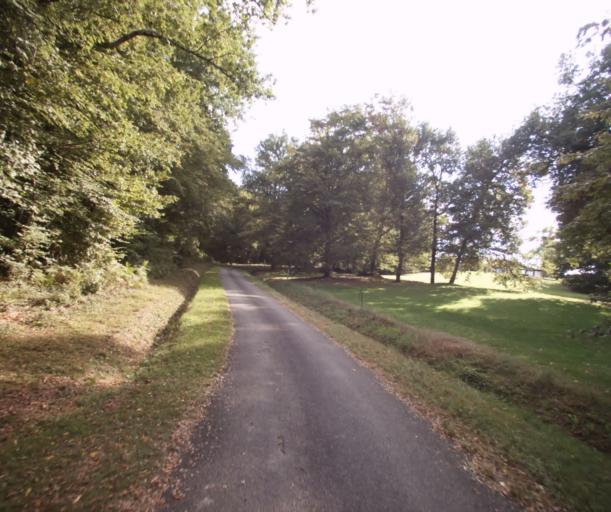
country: FR
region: Midi-Pyrenees
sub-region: Departement du Gers
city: Cazaubon
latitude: 43.9334
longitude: -0.0434
